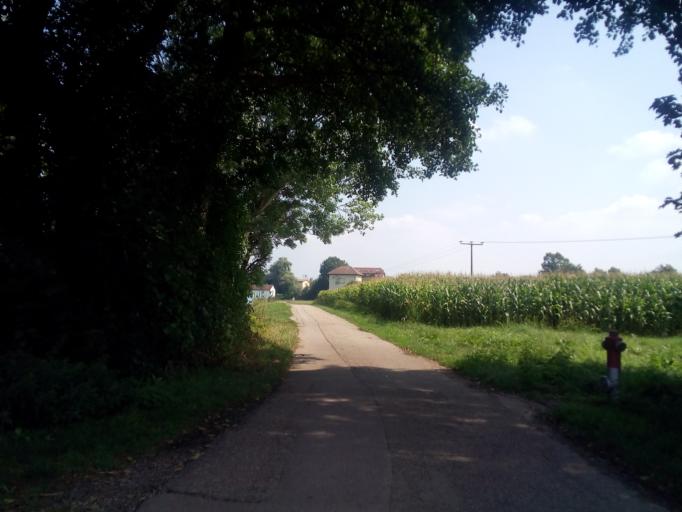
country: DE
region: Baden-Wuerttemberg
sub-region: Freiburg Region
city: Kehl
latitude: 48.6008
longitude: 7.8622
